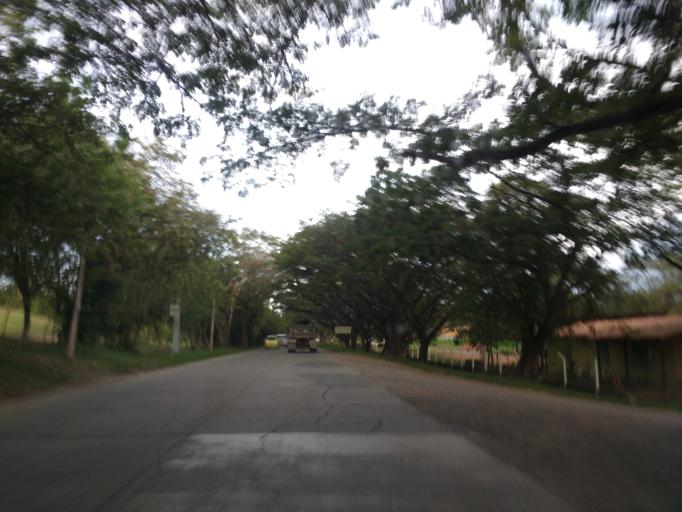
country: CO
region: Valle del Cauca
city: Cartago
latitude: 4.7553
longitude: -75.9402
